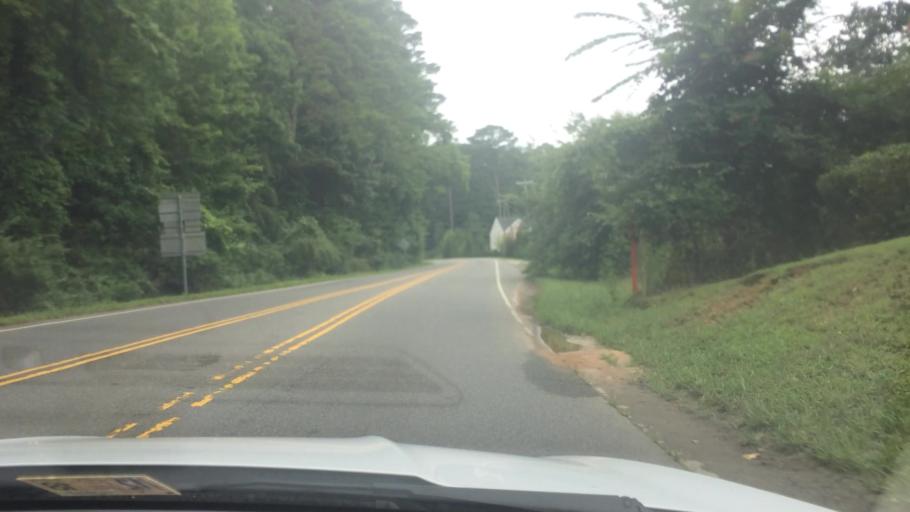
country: US
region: Virginia
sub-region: York County
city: Yorktown
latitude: 37.2333
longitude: -76.5335
